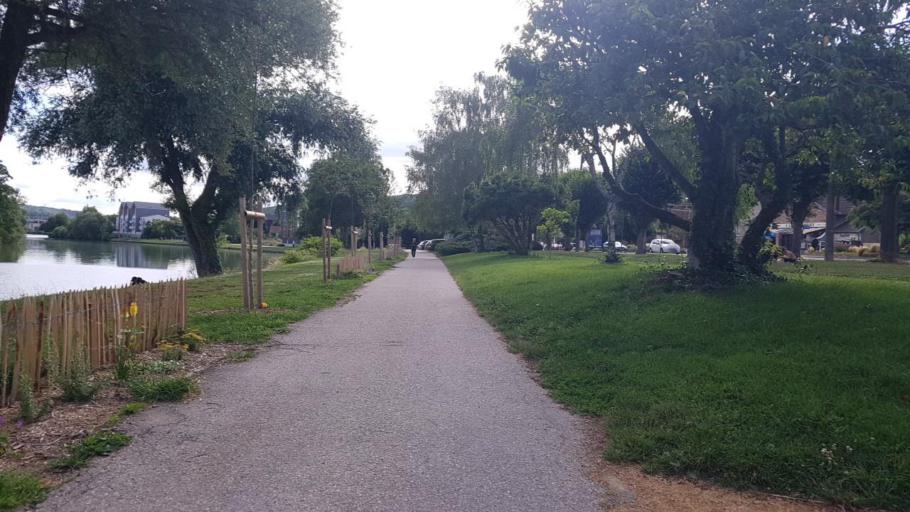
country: FR
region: Picardie
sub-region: Departement de l'Aisne
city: Chateau-Thierry
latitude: 49.0429
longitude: 3.3955
